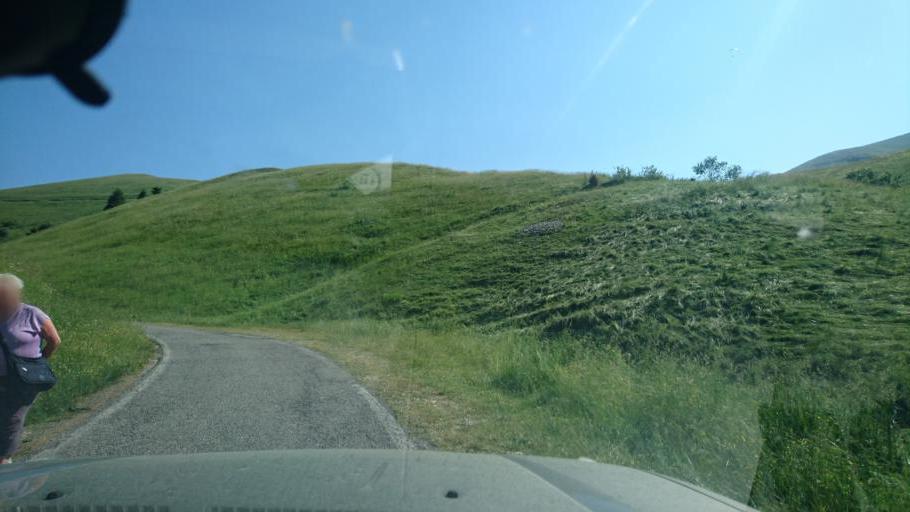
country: IT
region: Veneto
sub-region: Provincia di Treviso
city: Crespano del Grappa
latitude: 45.8865
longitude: 11.8362
